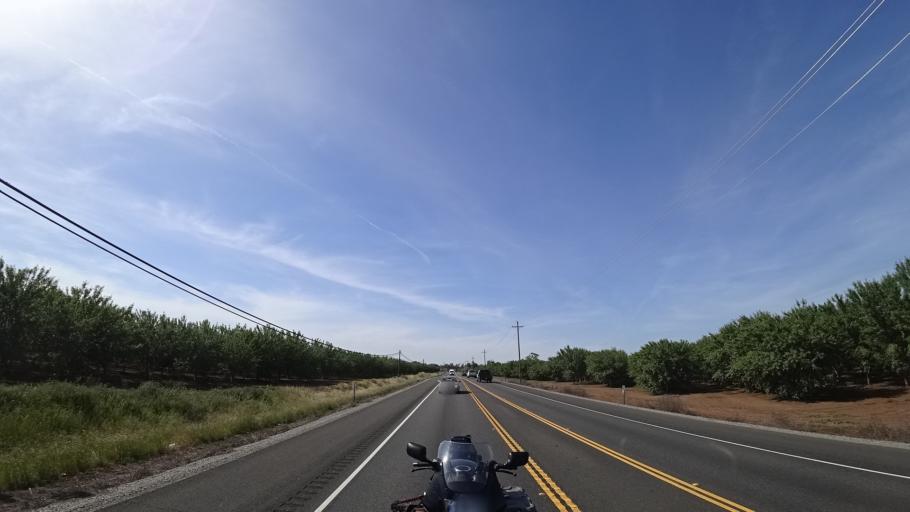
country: US
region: California
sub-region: Butte County
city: Chico
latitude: 39.7992
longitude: -121.9043
